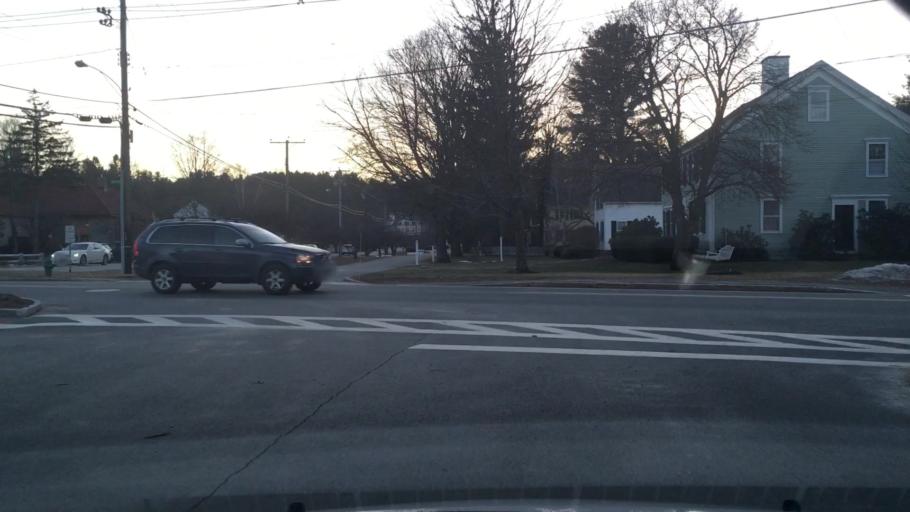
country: US
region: New Hampshire
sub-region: Hillsborough County
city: Milford
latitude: 42.8635
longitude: -71.6271
